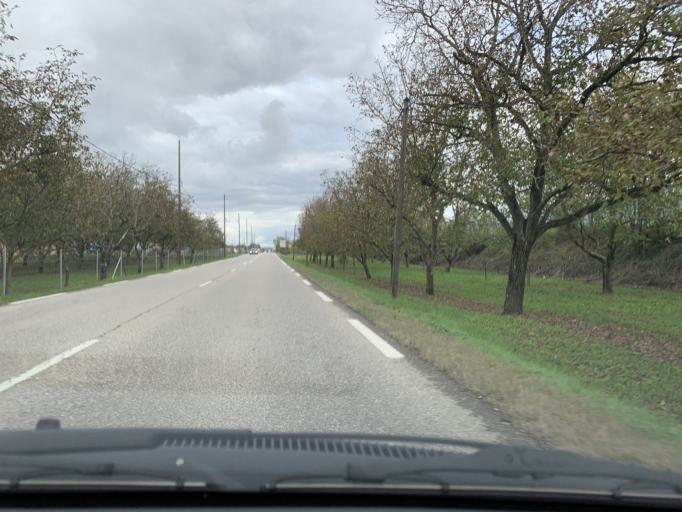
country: FR
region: Rhone-Alpes
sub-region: Departement de l'Isere
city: Chatte
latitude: 45.1199
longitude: 5.2740
